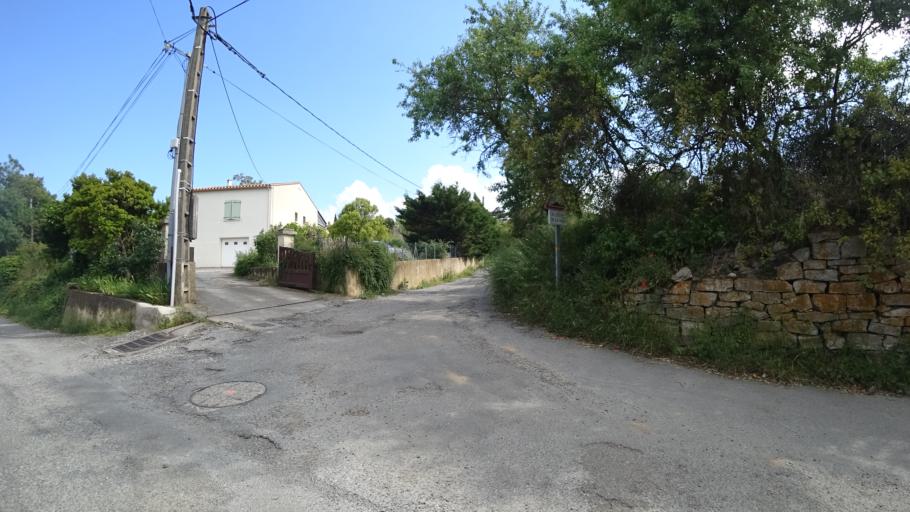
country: FR
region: Languedoc-Roussillon
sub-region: Departement de l'Aude
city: Ginestas
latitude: 43.2657
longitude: 2.8737
